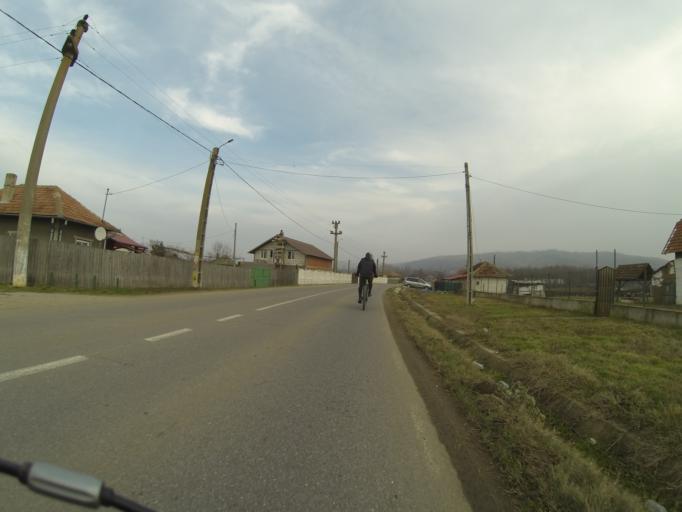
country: RO
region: Mehedinti
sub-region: Comuna Corlatel
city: Corlatel
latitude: 44.3981
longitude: 22.9248
